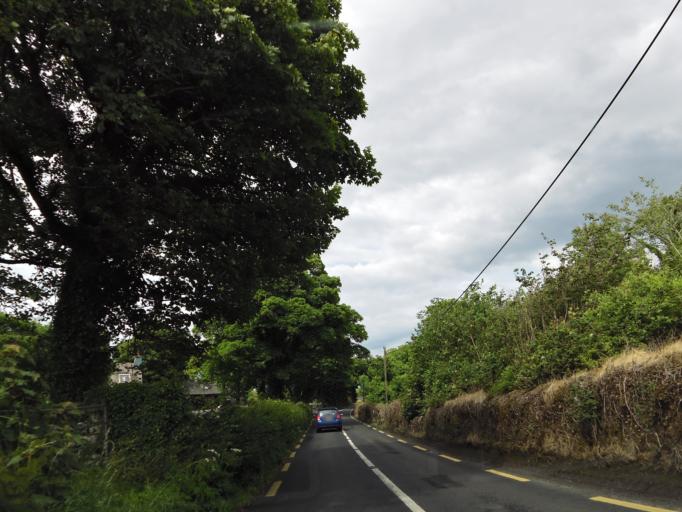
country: IE
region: Connaught
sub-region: County Galway
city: Bearna
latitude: 53.0895
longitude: -9.1736
